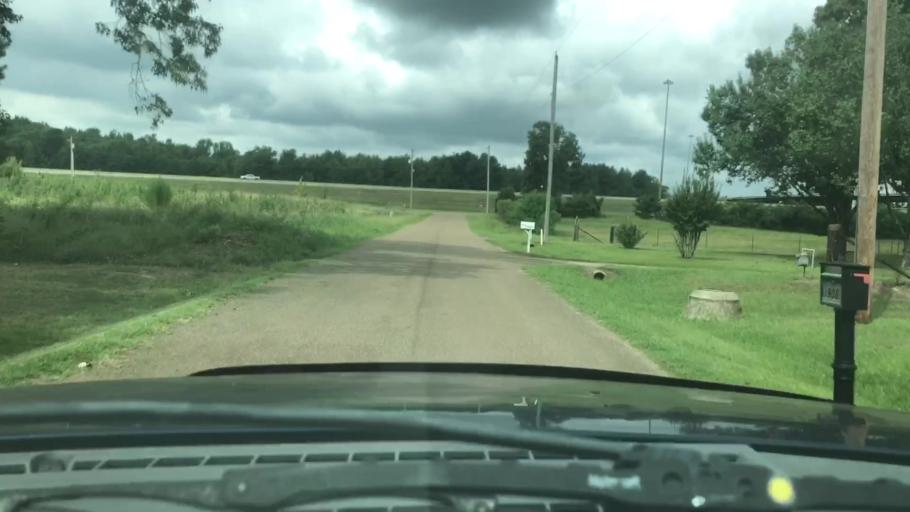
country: US
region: Texas
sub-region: Bowie County
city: Wake Village
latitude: 33.3915
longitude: -94.0949
